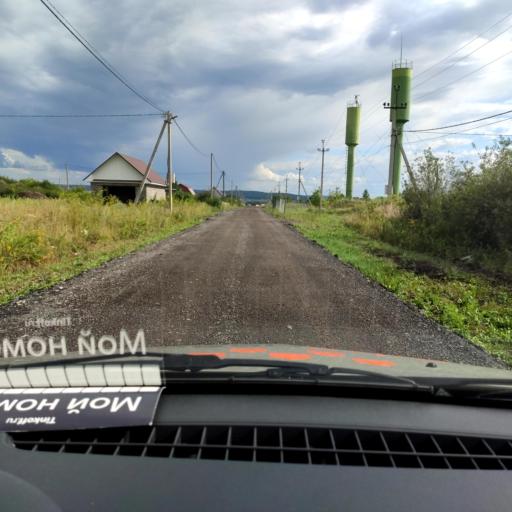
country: RU
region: Bashkortostan
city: Avdon
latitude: 54.5208
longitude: 55.8329
